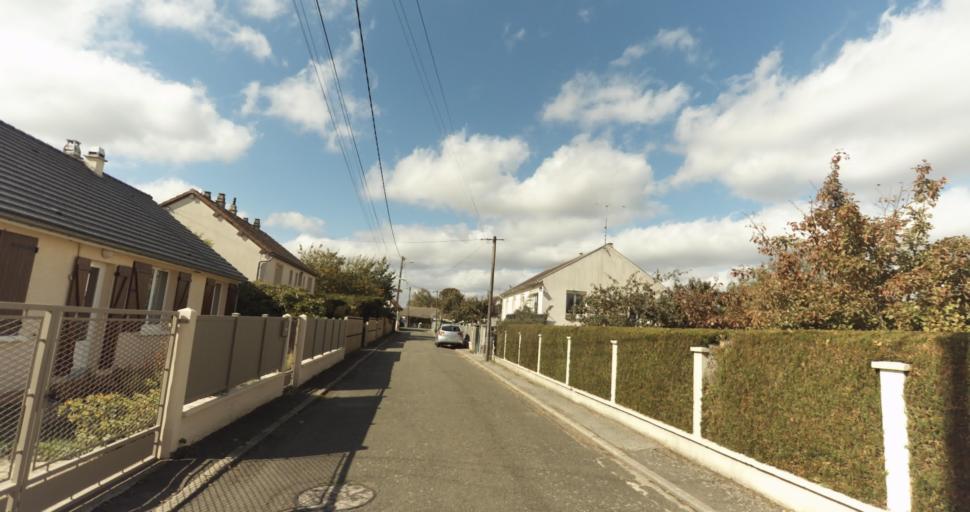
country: FR
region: Centre
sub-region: Departement d'Eure-et-Loir
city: Garnay
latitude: 48.7281
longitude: 1.3315
